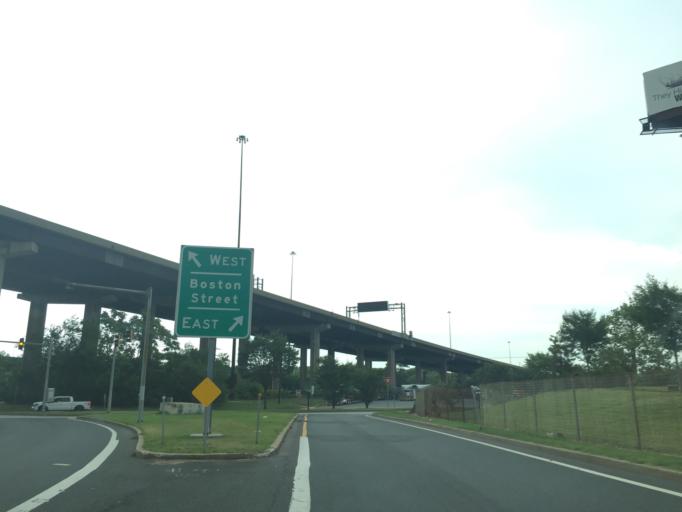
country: US
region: Maryland
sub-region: Baltimore County
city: Dundalk
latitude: 39.2778
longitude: -76.5507
